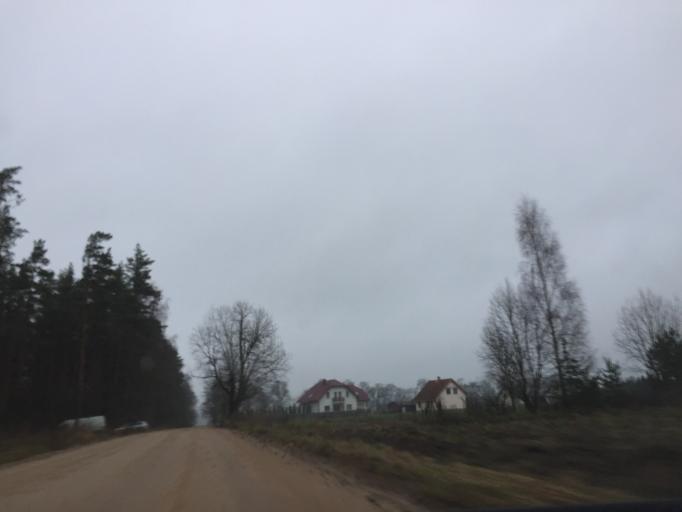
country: LV
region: Koceni
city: Koceni
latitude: 57.5372
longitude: 25.3334
